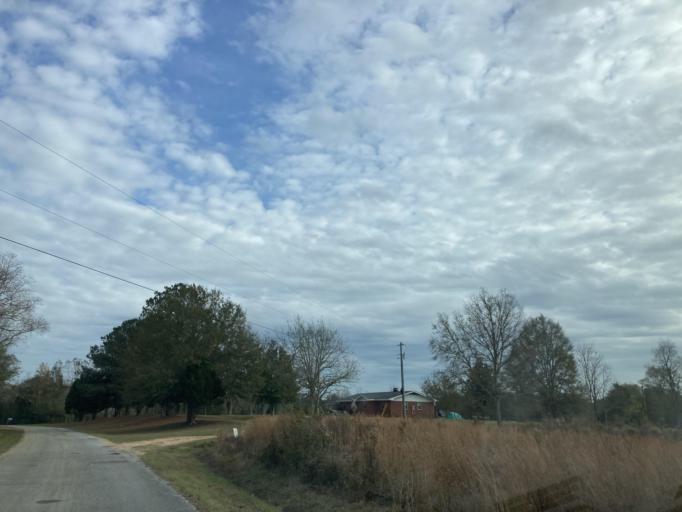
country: US
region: Mississippi
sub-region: Stone County
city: Wiggins
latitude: 30.9940
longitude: -89.2531
